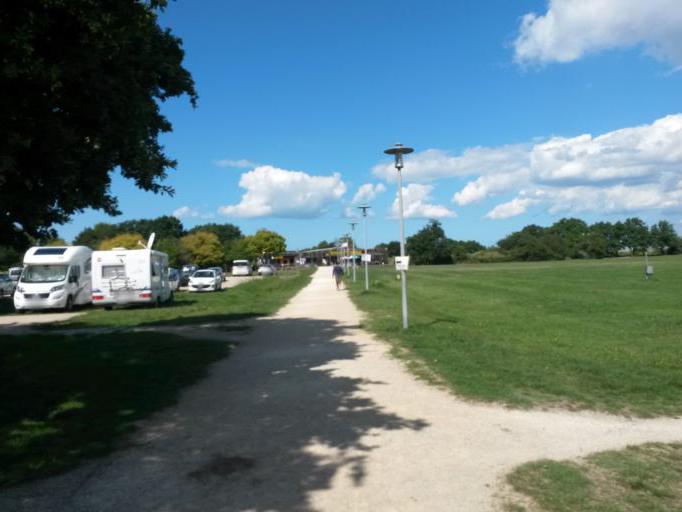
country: FR
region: Aquitaine
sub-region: Departement de la Gironde
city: Le Teich
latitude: 44.6404
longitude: -1.0190
